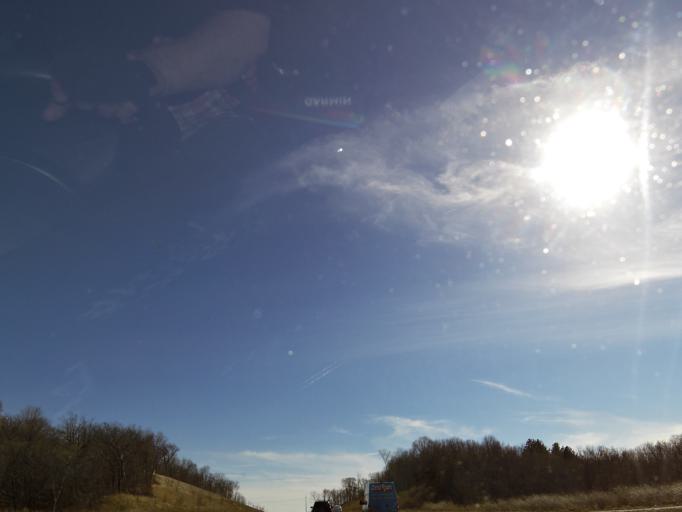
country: US
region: Minnesota
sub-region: Scott County
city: Prior Lake
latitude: 44.7587
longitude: -93.4397
